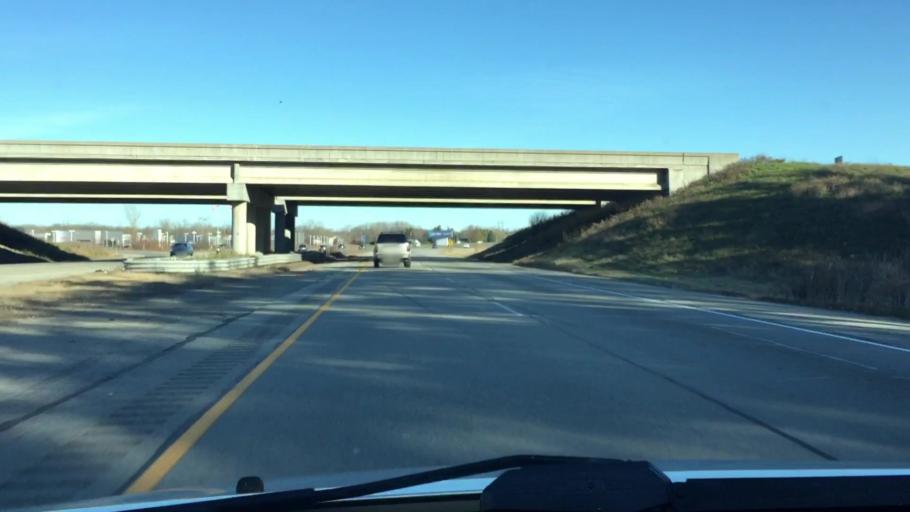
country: US
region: Wisconsin
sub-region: Outagamie County
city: Appleton
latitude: 44.2876
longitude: -88.4661
